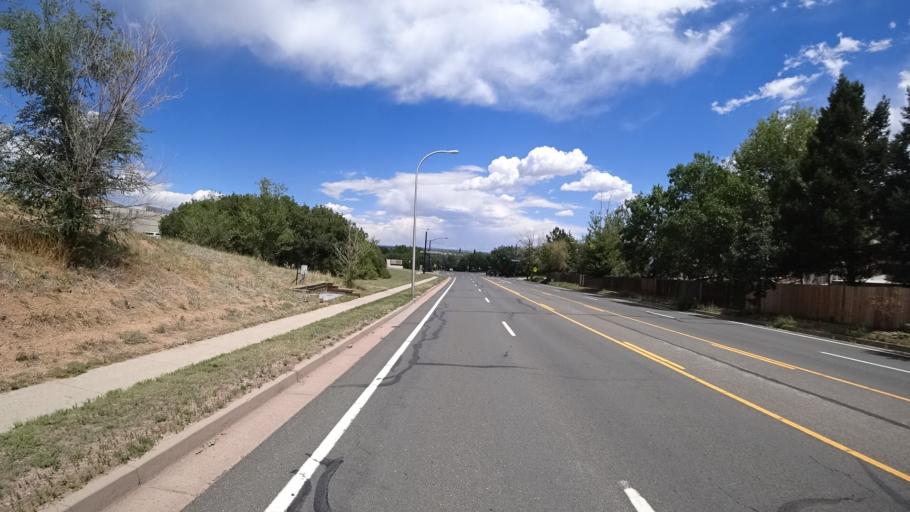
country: US
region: Colorado
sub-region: El Paso County
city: Stratmoor
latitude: 38.7822
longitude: -104.8011
